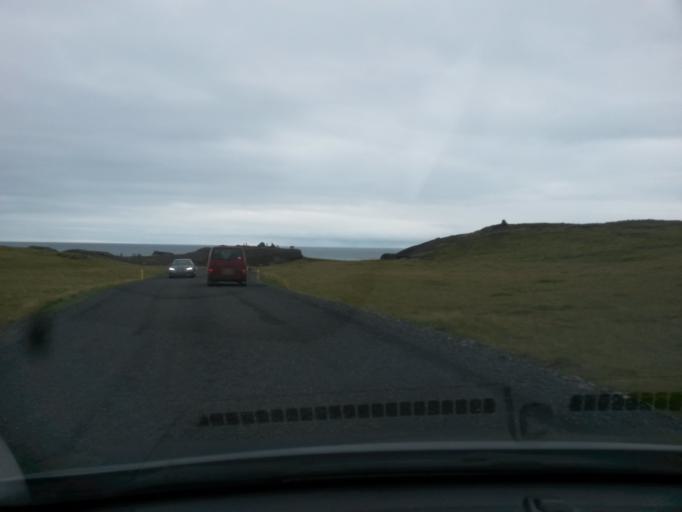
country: IS
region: South
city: Vestmannaeyjar
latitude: 63.4051
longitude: -19.1075
